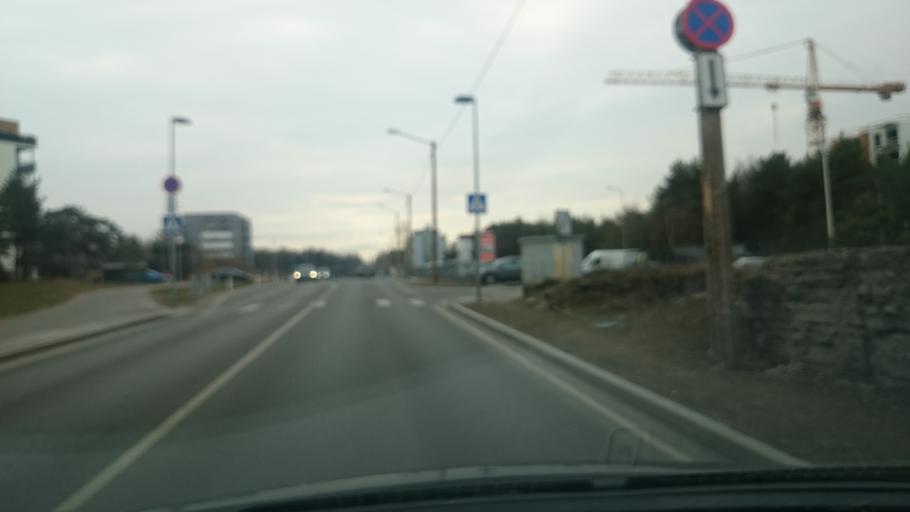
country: EE
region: Harju
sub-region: Saue vald
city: Laagri
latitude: 59.3974
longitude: 24.6451
